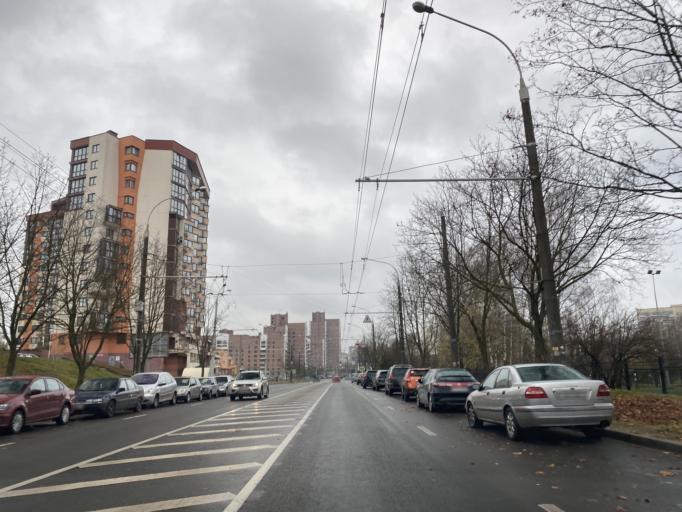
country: BY
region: Minsk
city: Bal'shavik
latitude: 53.9567
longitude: 27.6124
